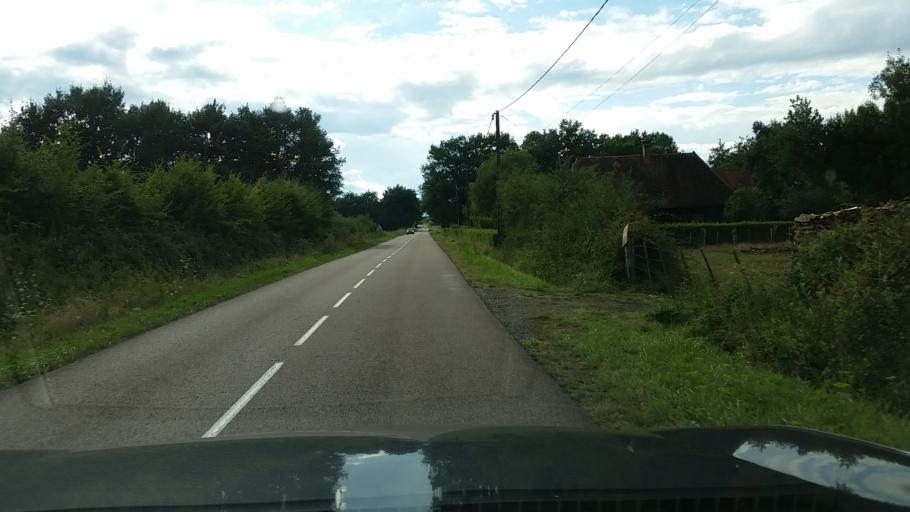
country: FR
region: Bourgogne
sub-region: Departement de Saone-et-Loire
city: Saint-Germain-du-Bois
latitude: 46.7340
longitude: 5.2669
